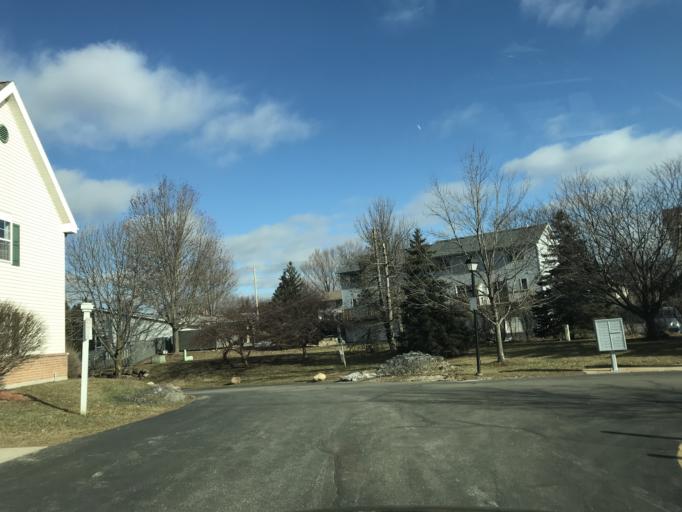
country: US
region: Wisconsin
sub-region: Dane County
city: Monona
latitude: 43.1087
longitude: -89.2974
